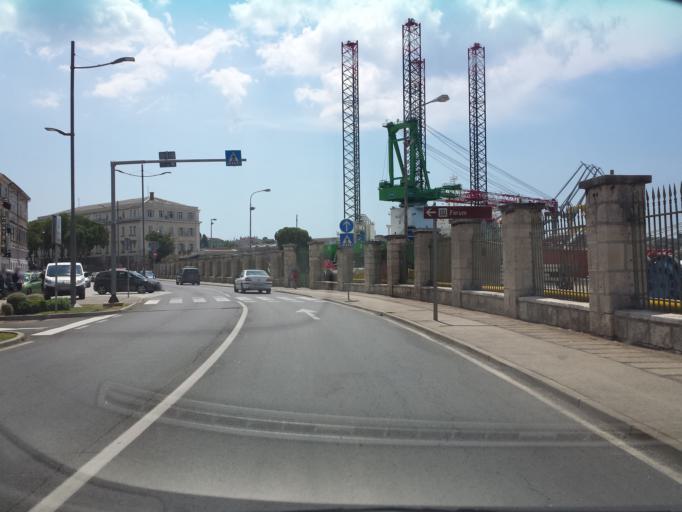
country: HR
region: Istarska
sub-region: Grad Pula
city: Pula
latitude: 44.8700
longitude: 13.8414
